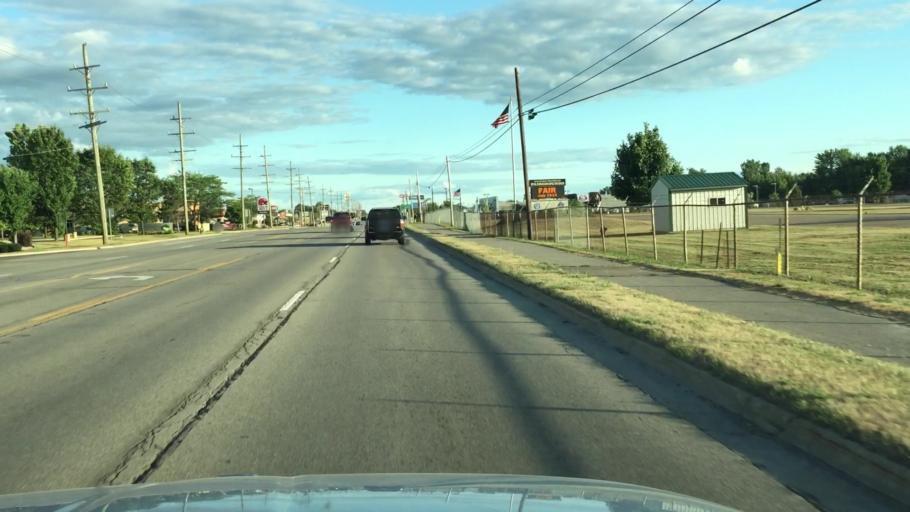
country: US
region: Michigan
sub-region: Lapeer County
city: Imlay City
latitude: 43.0162
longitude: -83.0720
